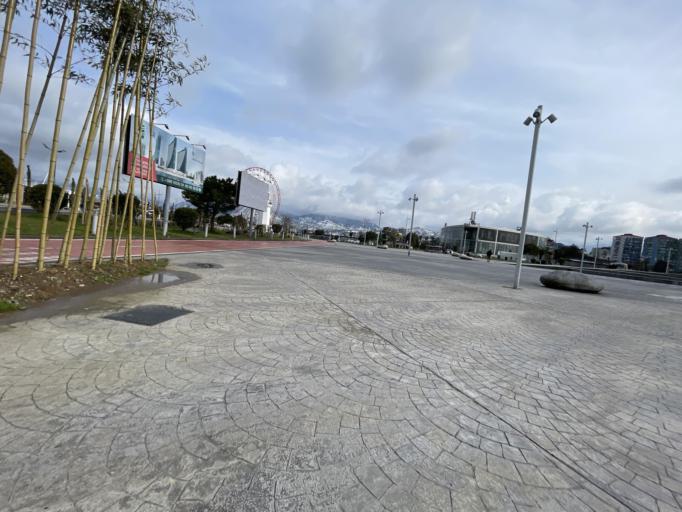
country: GE
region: Ajaria
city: Batumi
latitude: 41.6565
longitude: 41.6399
